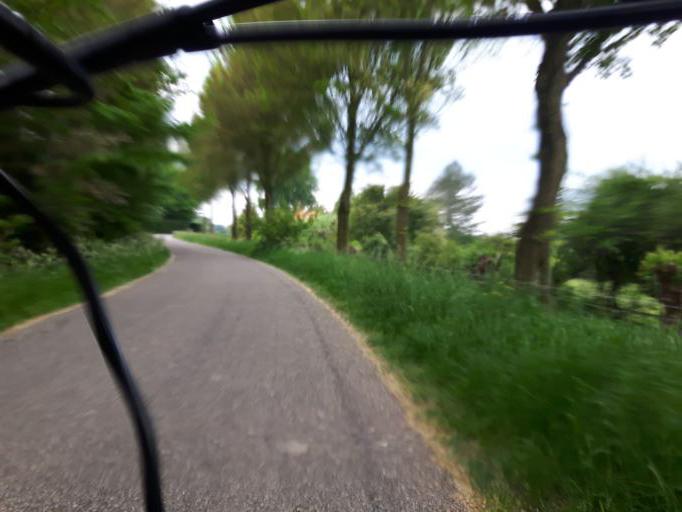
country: NL
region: Zeeland
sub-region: Gemeente Goes
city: Goes
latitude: 51.4390
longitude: 3.8340
